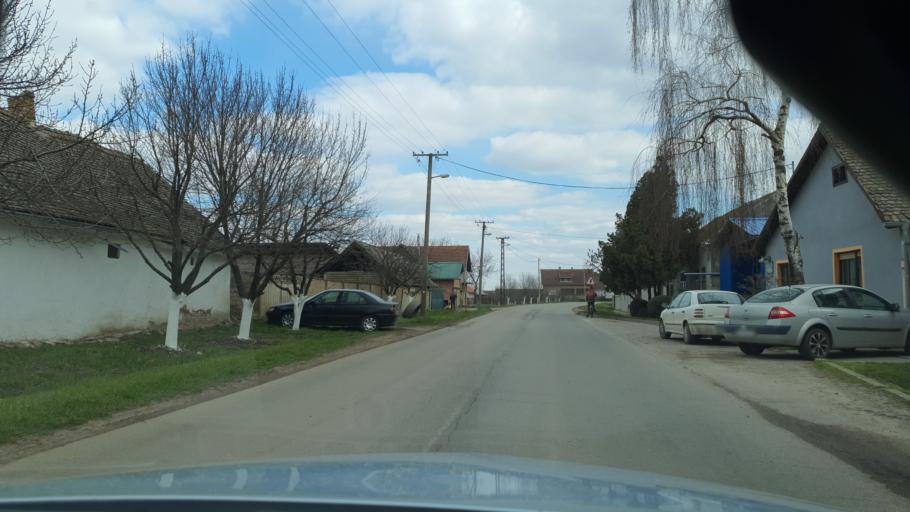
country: RS
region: Autonomna Pokrajina Vojvodina
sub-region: Zapadnobacki Okrug
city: Odzaci
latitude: 45.4507
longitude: 19.3412
